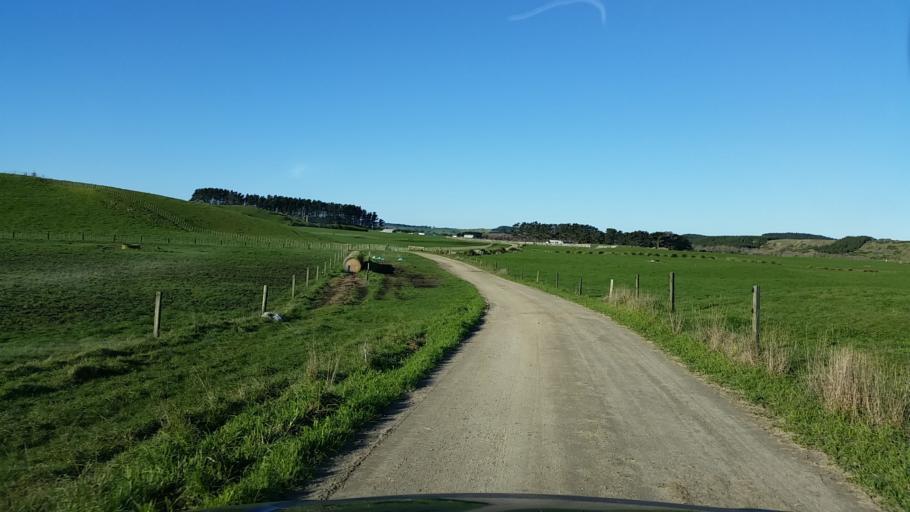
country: NZ
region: Taranaki
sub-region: South Taranaki District
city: Patea
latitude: -39.8379
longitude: 174.6946
